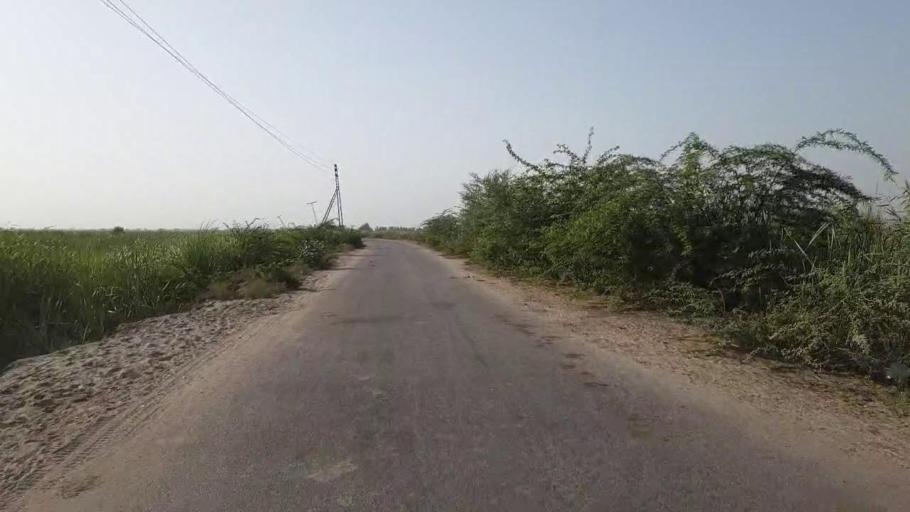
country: PK
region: Sindh
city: Jam Sahib
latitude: 26.4069
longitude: 68.8769
